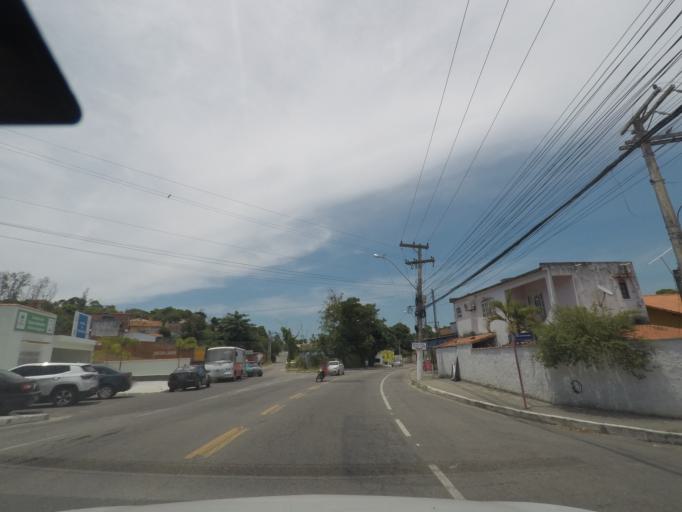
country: BR
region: Rio de Janeiro
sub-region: Marica
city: Marica
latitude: -22.9289
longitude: -42.8211
